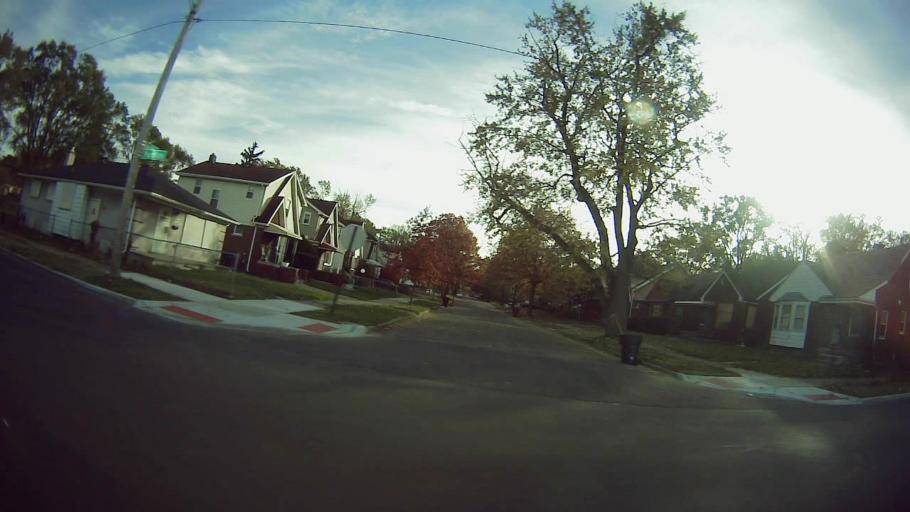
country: US
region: Michigan
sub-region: Oakland County
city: Oak Park
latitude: 42.4090
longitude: -83.1917
